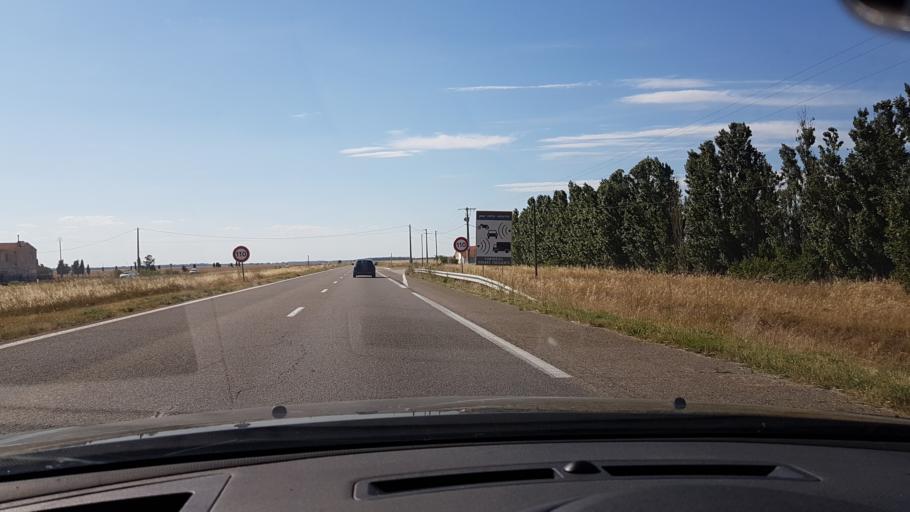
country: FR
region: Provence-Alpes-Cote d'Azur
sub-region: Departement des Bouches-du-Rhone
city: Fos-sur-Mer
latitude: 43.5048
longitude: 4.8636
